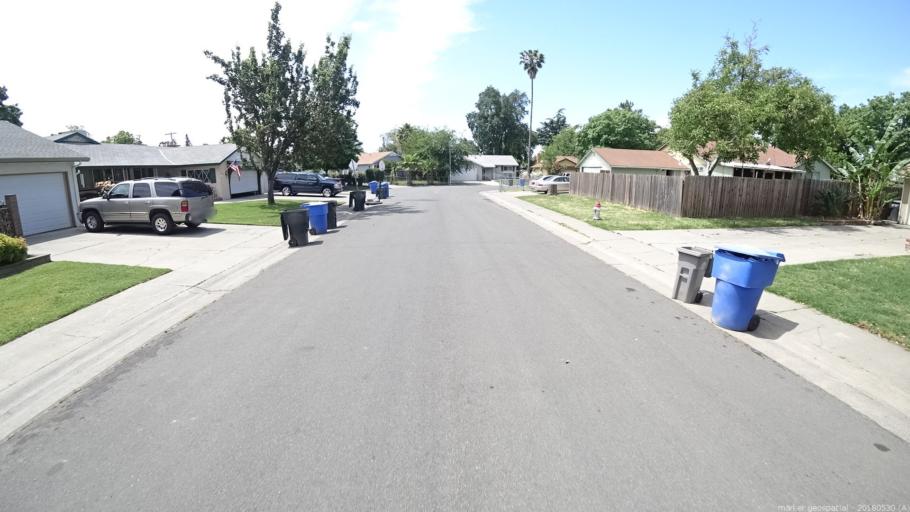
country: US
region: California
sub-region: Sacramento County
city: Sacramento
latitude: 38.6232
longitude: -121.4790
